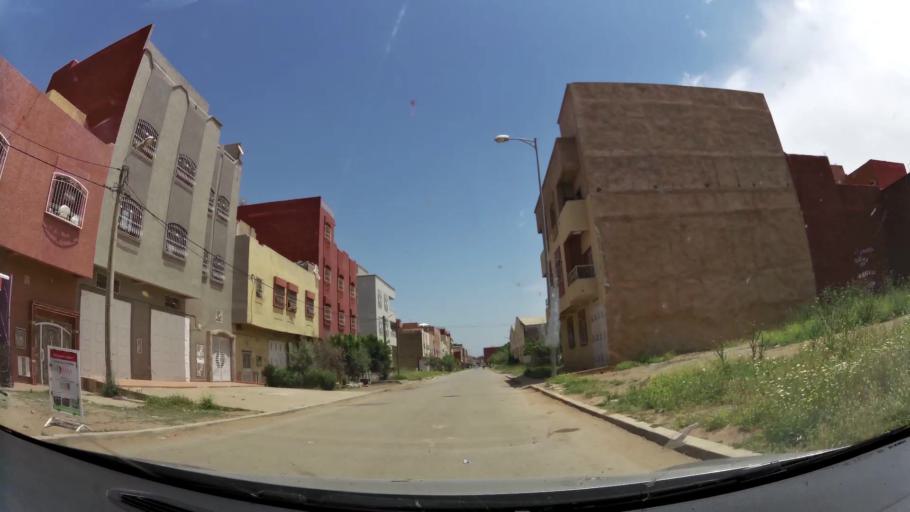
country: MA
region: Rabat-Sale-Zemmour-Zaer
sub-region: Khemisset
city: Khemisset
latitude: 33.8246
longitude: -6.0832
